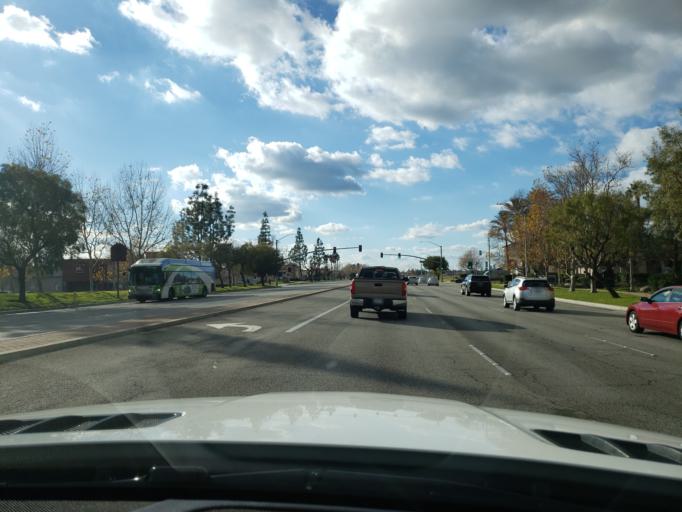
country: US
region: California
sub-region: San Bernardino County
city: Rancho Cucamonga
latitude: 34.1064
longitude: -117.5477
